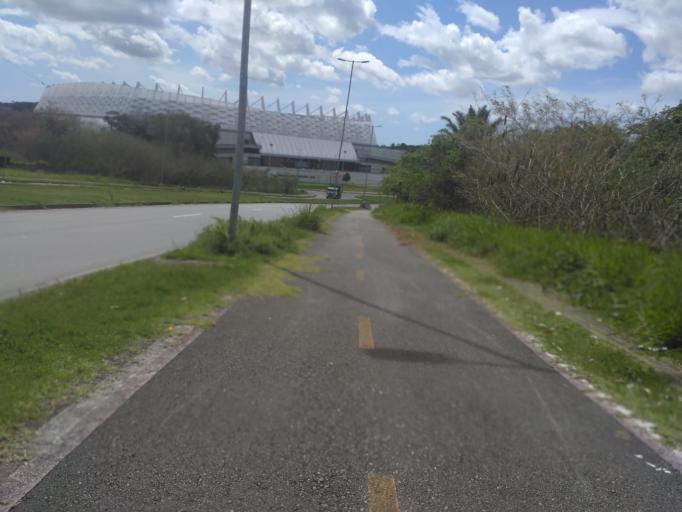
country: BR
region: Pernambuco
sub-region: Sao Lourenco Da Mata
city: Sao Lourenco da Mata
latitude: -8.0443
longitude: -35.0103
